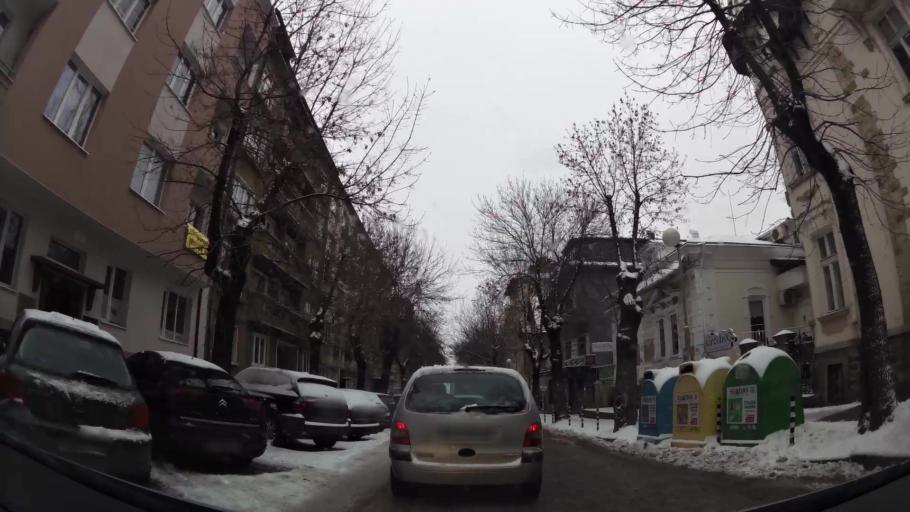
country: BG
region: Sofia-Capital
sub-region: Stolichna Obshtina
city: Sofia
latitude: 42.6928
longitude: 23.3429
